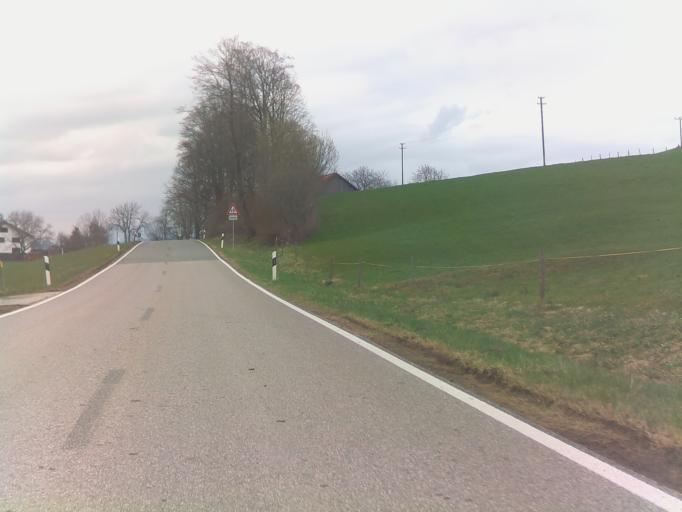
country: DE
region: Bavaria
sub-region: Upper Bavaria
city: Uffing
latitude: 47.7126
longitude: 11.1059
